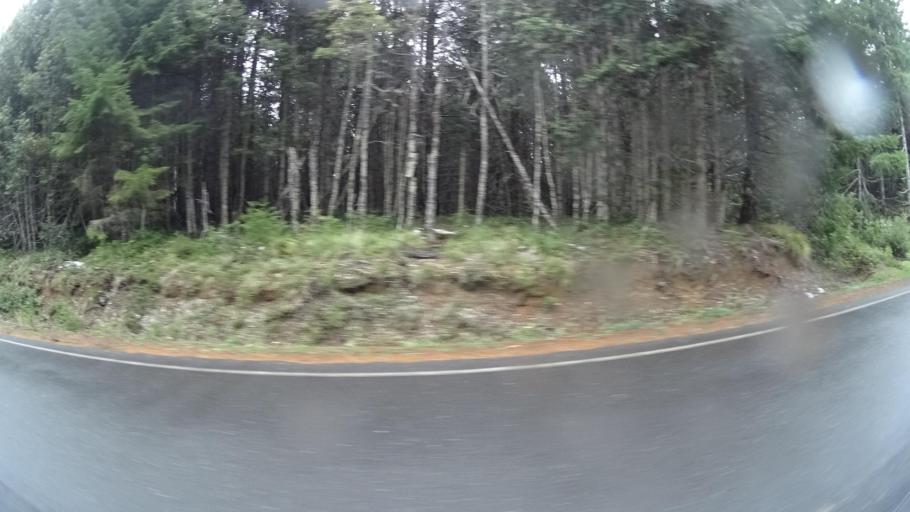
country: US
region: California
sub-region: Humboldt County
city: Willow Creek
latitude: 41.1718
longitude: -123.8132
